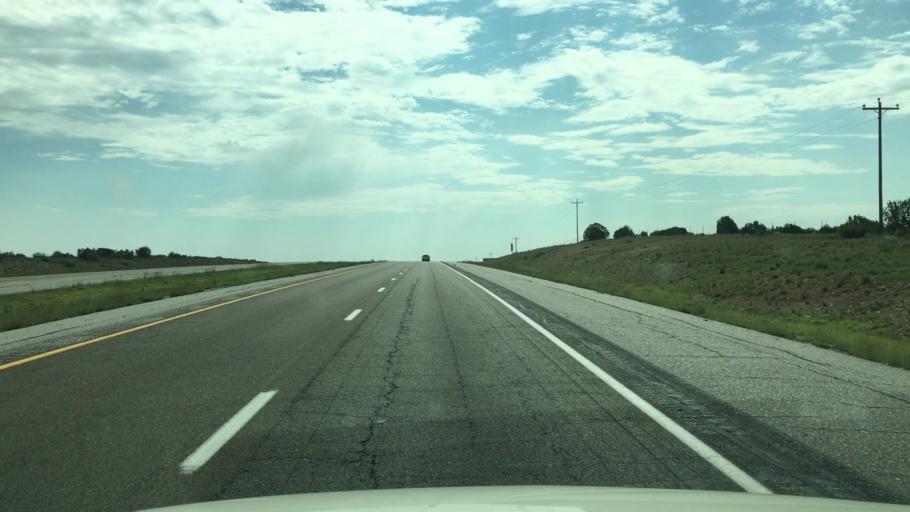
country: US
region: New Mexico
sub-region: San Miguel County
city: Las Vegas
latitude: 34.9973
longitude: -105.4197
